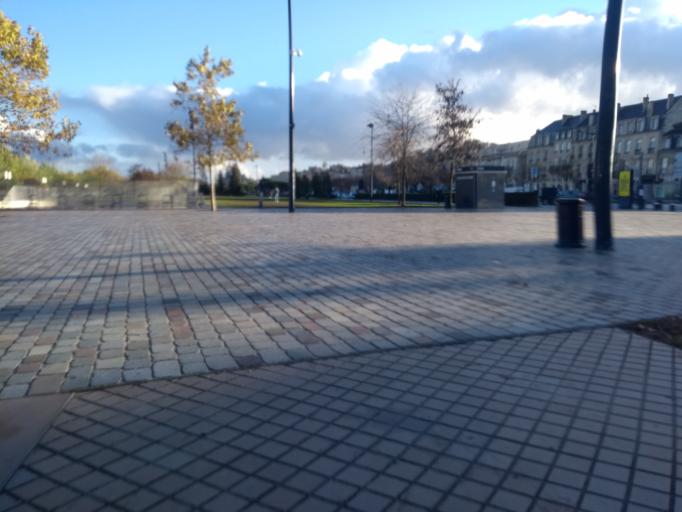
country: FR
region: Aquitaine
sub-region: Departement de la Gironde
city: Bordeaux
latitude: 44.8353
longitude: -0.5633
